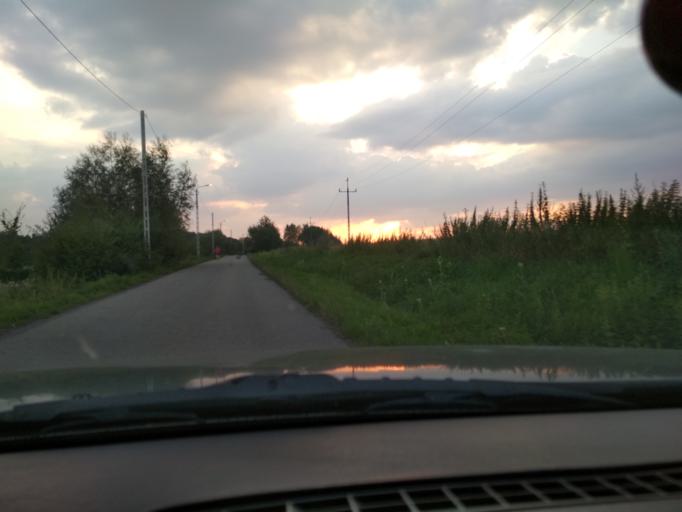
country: PL
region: Silesian Voivodeship
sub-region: Powiat bielski
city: Jasienica
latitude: 49.8391
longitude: 18.9335
